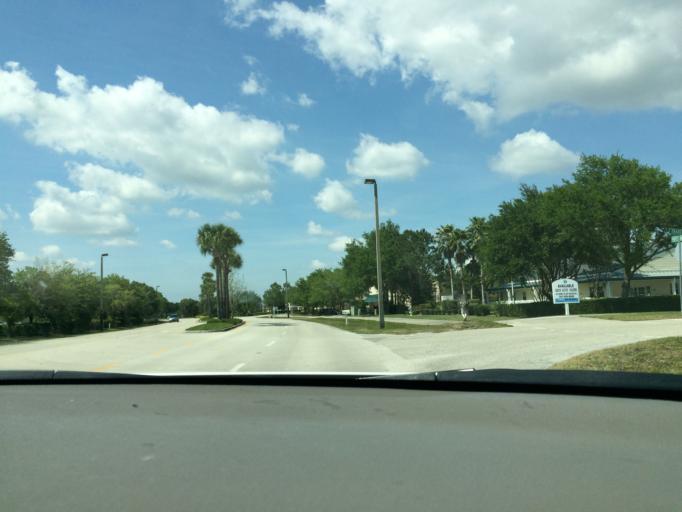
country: US
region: Florida
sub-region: Sarasota County
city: The Meadows
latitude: 27.3811
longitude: -82.4245
